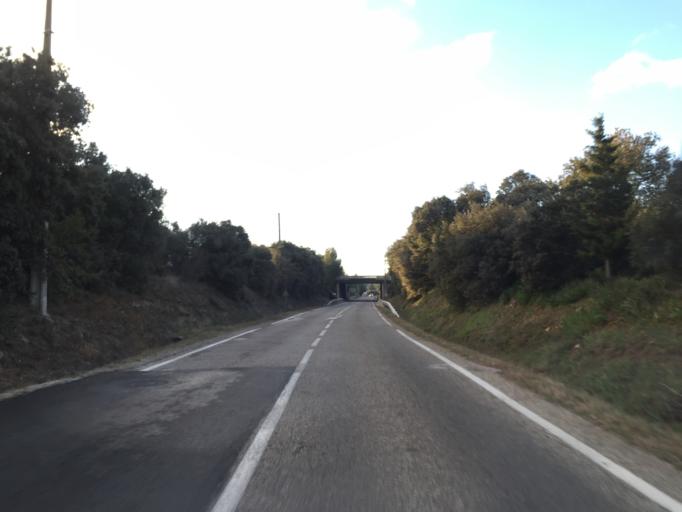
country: FR
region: Provence-Alpes-Cote d'Azur
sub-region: Departement du Vaucluse
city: Orange
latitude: 44.1143
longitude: 4.8202
